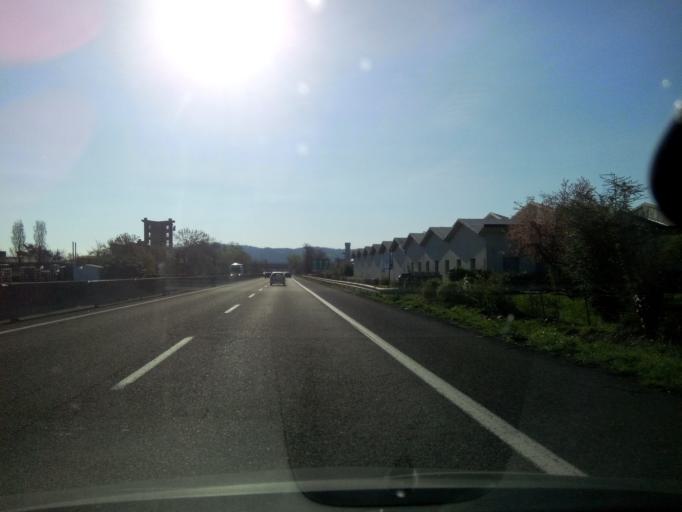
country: IT
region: Emilia-Romagna
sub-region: Provincia di Bologna
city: Riale
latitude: 44.4936
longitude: 11.2387
